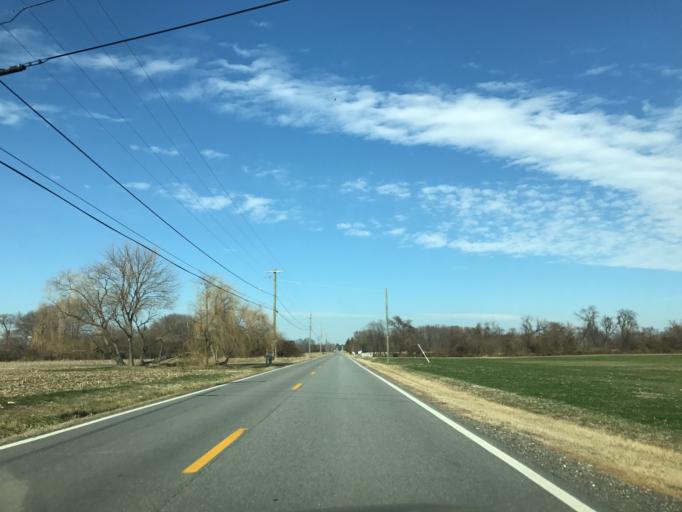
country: US
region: Maryland
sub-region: Queen Anne's County
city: Stevensville
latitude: 39.0163
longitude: -76.3114
